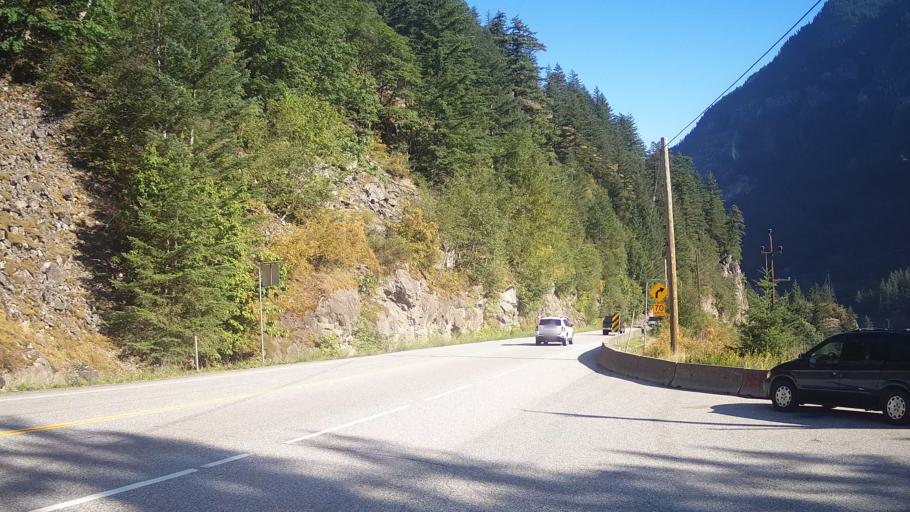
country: CA
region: British Columbia
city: Hope
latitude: 49.5764
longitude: -121.4029
